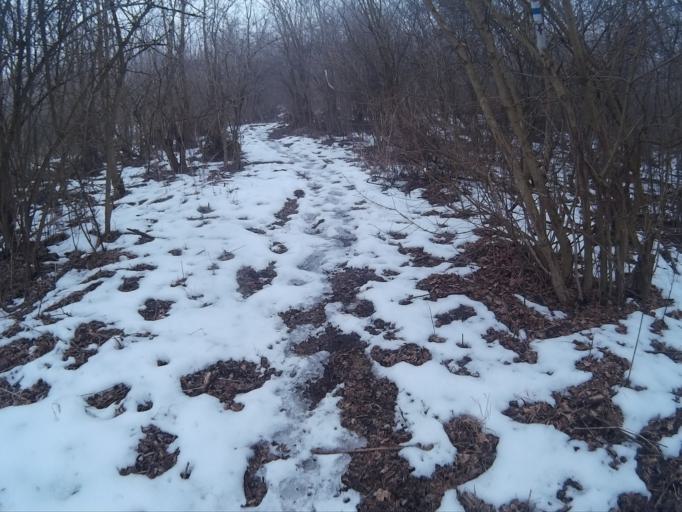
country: HU
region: Nograd
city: Matraverebely
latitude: 47.9784
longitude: 19.7639
